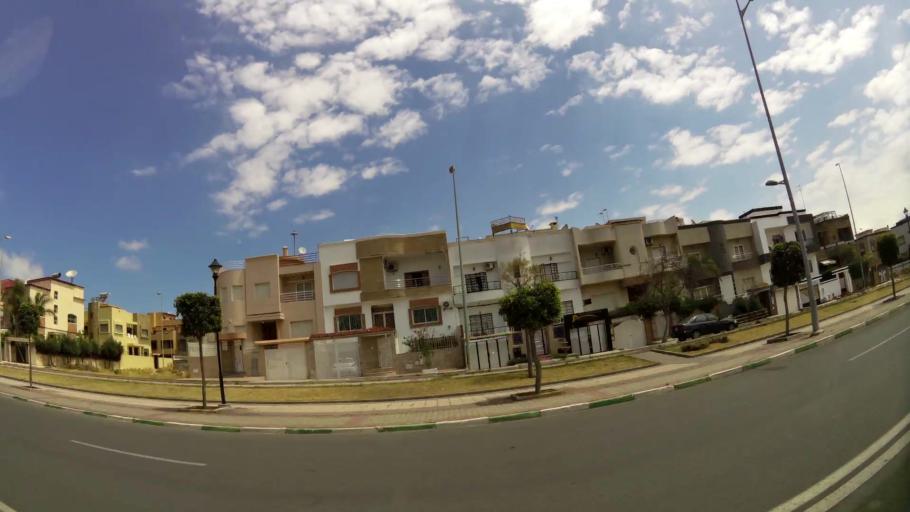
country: MA
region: Gharb-Chrarda-Beni Hssen
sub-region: Kenitra Province
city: Kenitra
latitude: 34.2728
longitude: -6.6066
